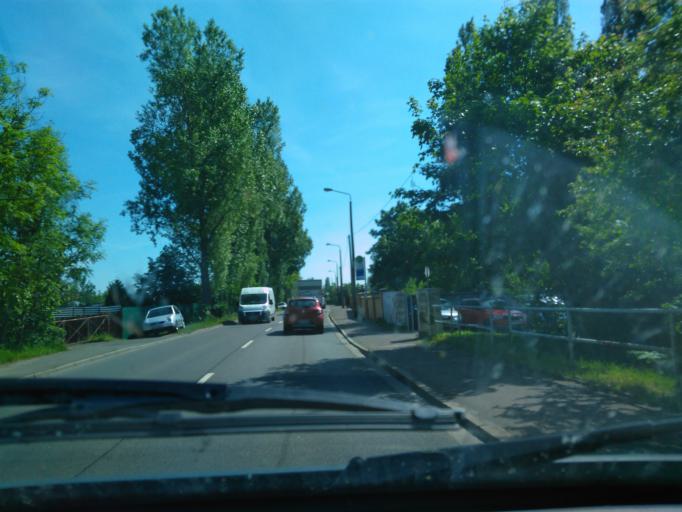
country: DE
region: Saxony
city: Taucha
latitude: 51.3563
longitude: 12.4443
